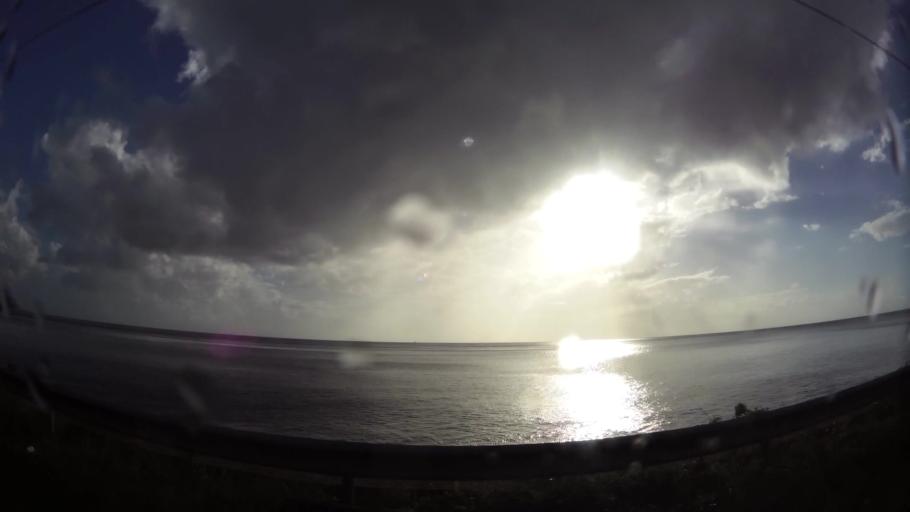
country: DM
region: Saint Joseph
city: Saint Joseph
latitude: 15.3869
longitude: -61.4145
